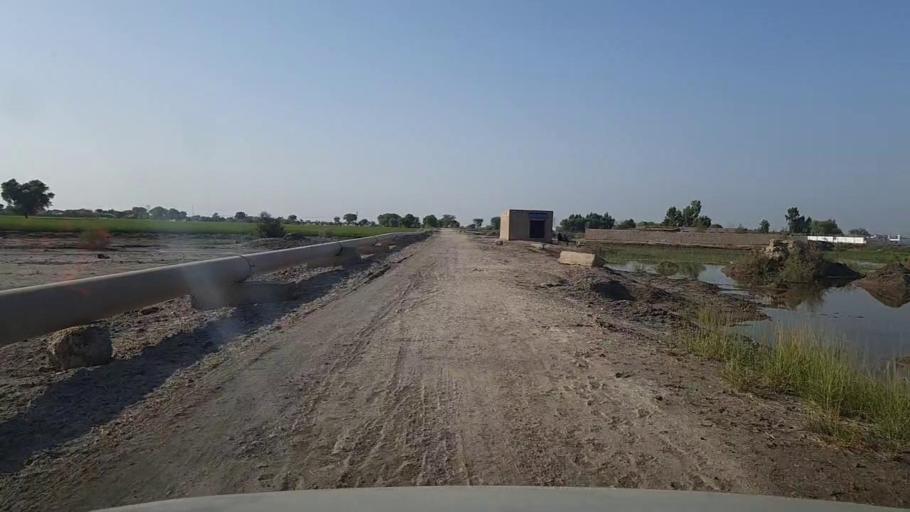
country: PK
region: Sindh
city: Kandhkot
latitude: 28.2852
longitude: 69.3339
